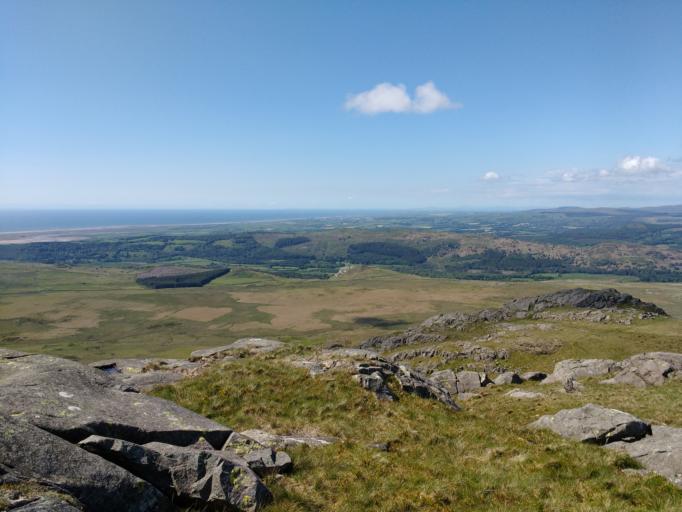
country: GB
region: England
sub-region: Cumbria
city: Millom
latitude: 54.3492
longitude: -3.3081
